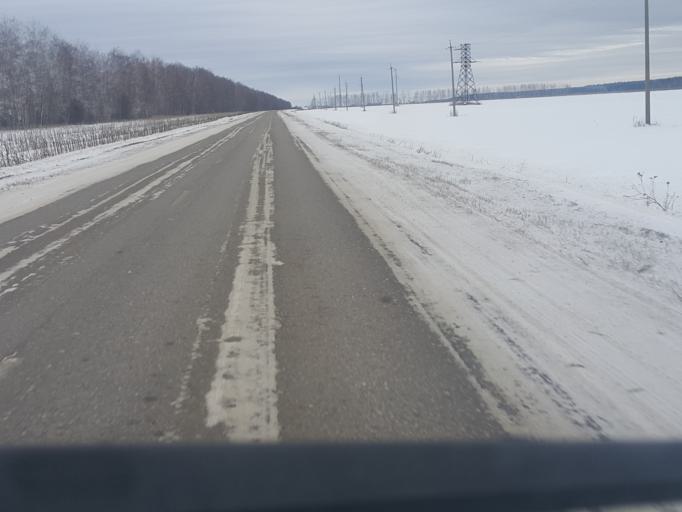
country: RU
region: Tambov
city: Rasskazovo
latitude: 52.8249
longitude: 41.8026
